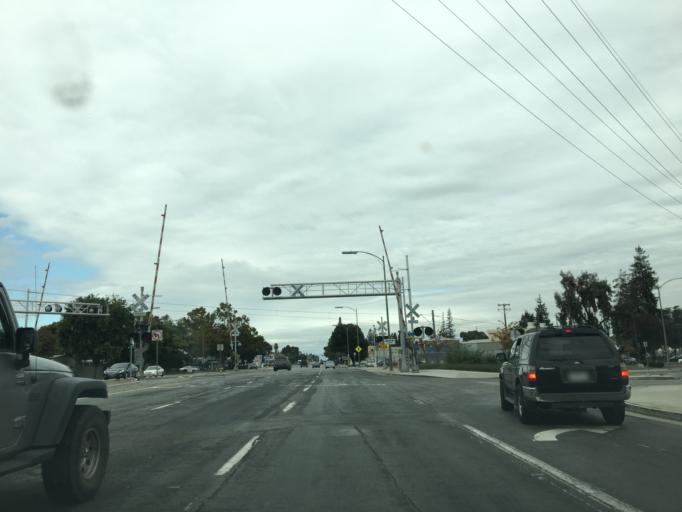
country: US
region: California
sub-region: Santa Clara County
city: Campbell
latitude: 37.2976
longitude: -121.9316
